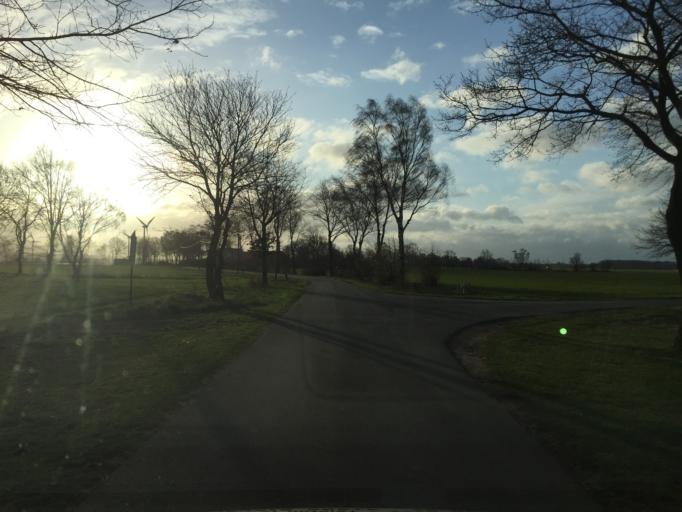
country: DE
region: Lower Saxony
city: Borstel
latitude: 52.6144
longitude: 8.9335
